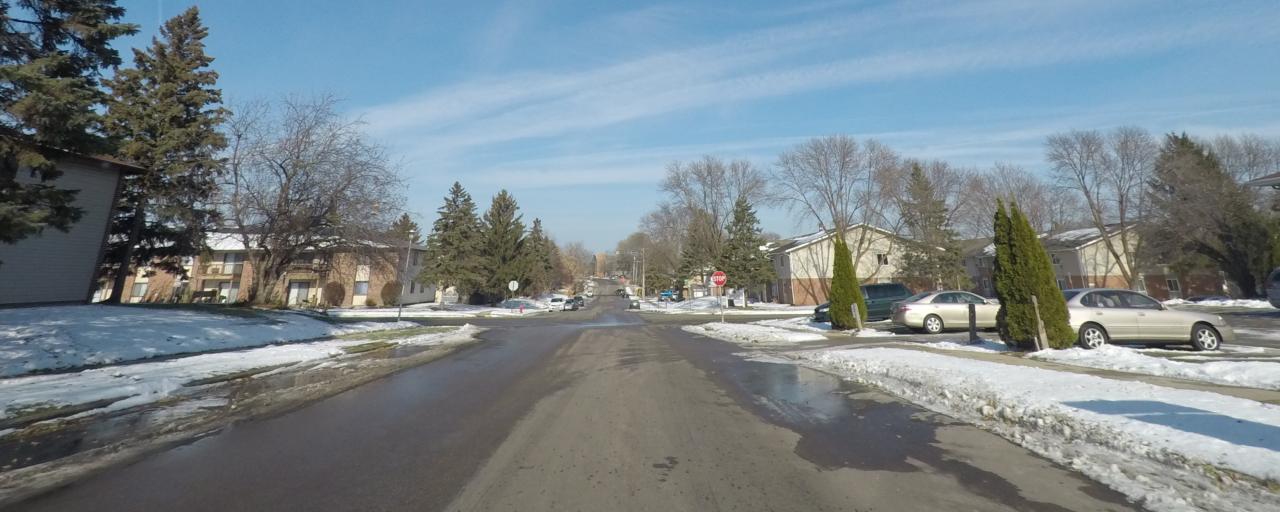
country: US
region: Wisconsin
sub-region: Dane County
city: Madison
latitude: 43.0289
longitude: -89.4147
